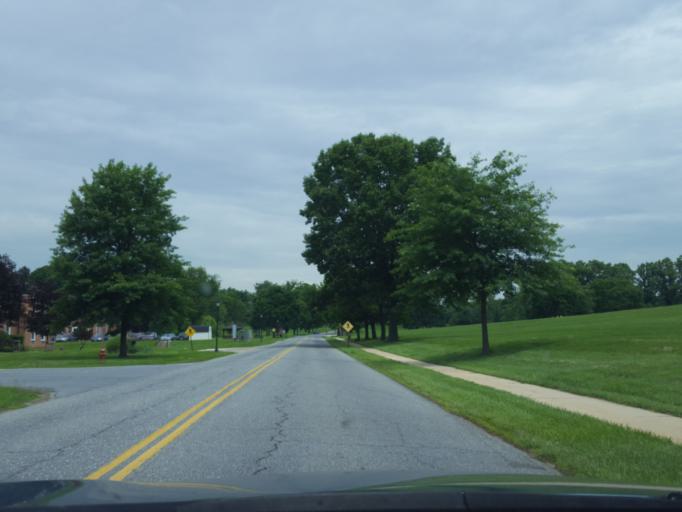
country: US
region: Maryland
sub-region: Carroll County
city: Sykesville
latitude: 39.3858
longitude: -76.9596
